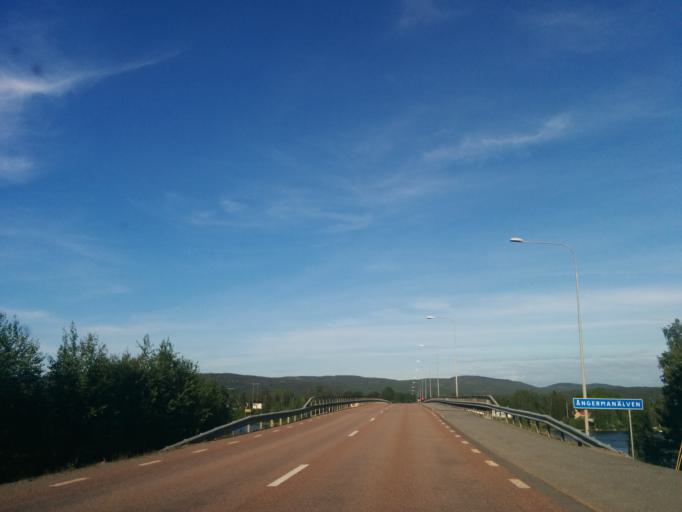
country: SE
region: Vaesternorrland
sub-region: Kramfors Kommun
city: Kramfors
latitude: 63.0233
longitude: 17.7780
